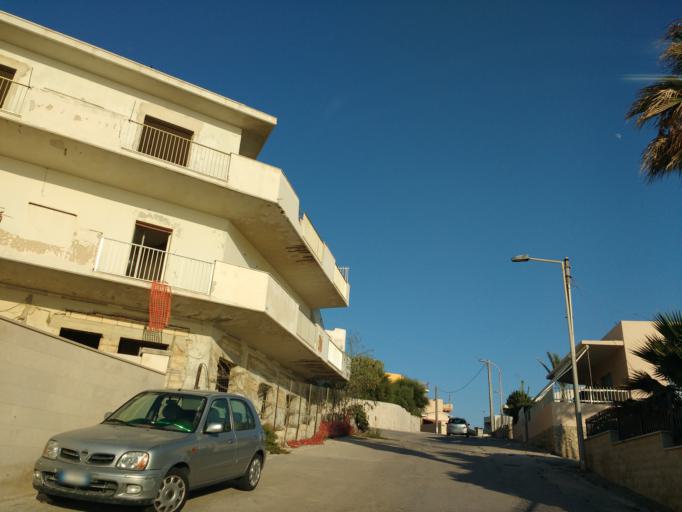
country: IT
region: Sicily
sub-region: Ragusa
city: Cava d'Aliga
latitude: 36.7313
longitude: 14.6819
